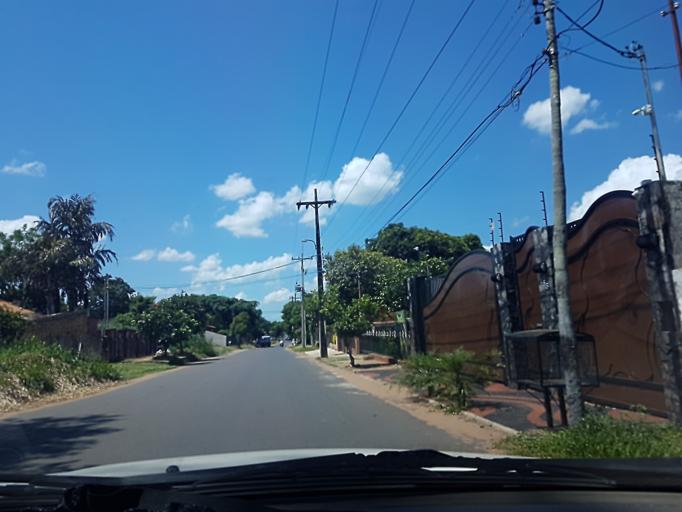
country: PY
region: Central
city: San Lorenzo
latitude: -25.2598
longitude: -57.4952
